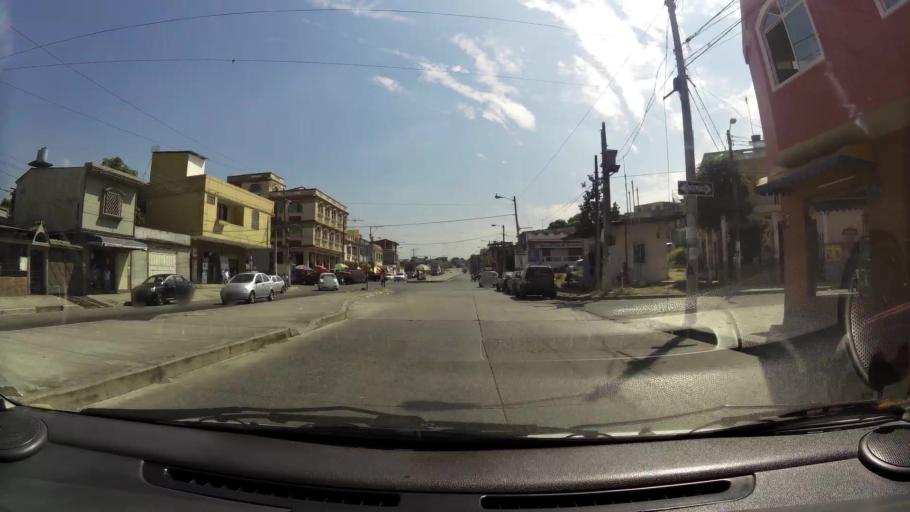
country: EC
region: Guayas
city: Eloy Alfaro
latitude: -2.1261
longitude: -79.9118
